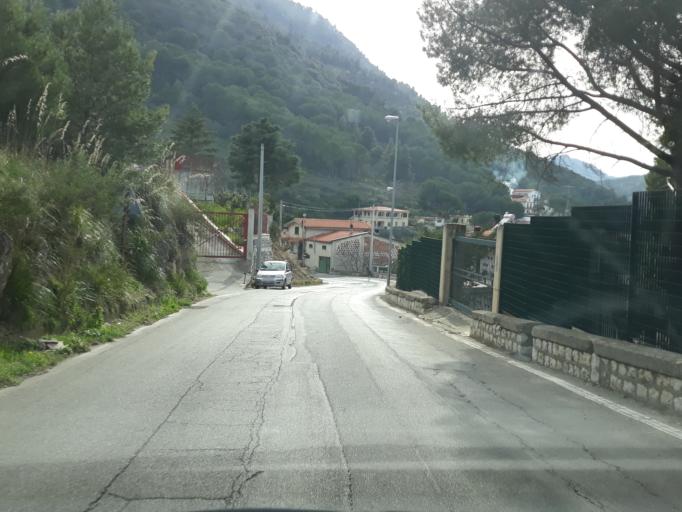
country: IT
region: Sicily
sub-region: Palermo
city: Altofonte
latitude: 38.0424
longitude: 13.3024
